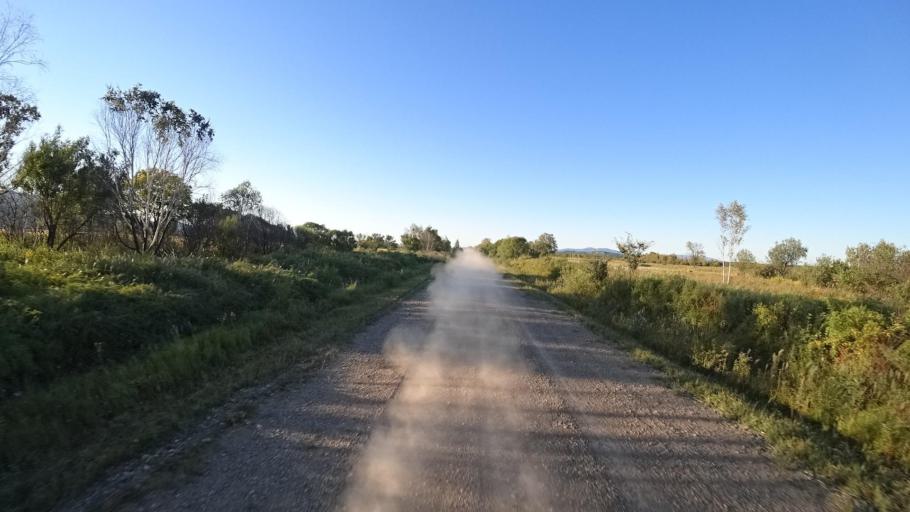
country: RU
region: Primorskiy
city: Kirovskiy
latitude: 44.7967
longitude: 133.6218
